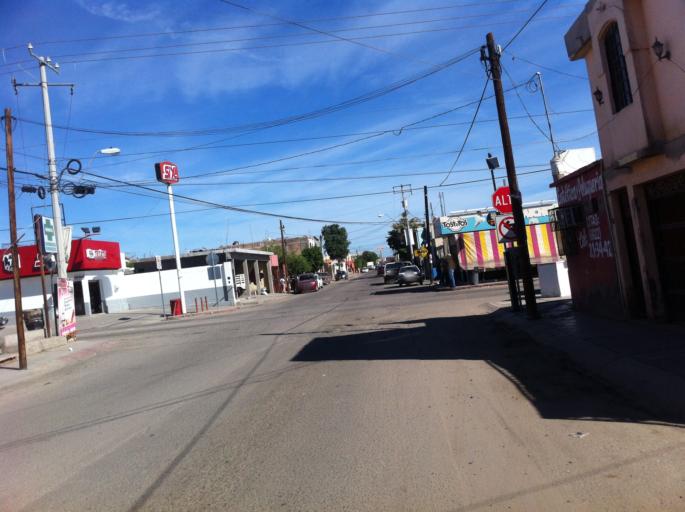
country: MX
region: Sonora
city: Hermosillo
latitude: 29.1003
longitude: -111.0162
